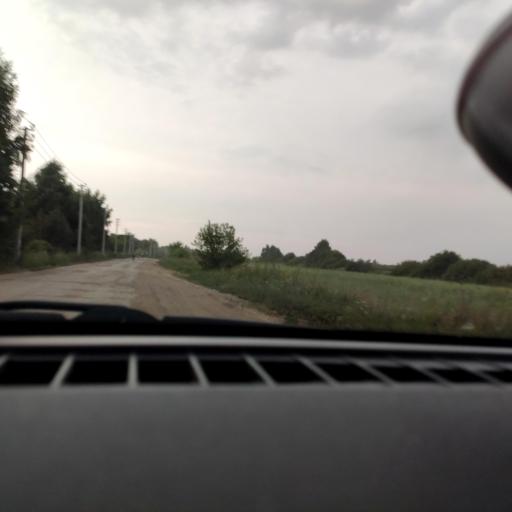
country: RU
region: Perm
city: Kondratovo
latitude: 57.9963
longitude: 55.9967
